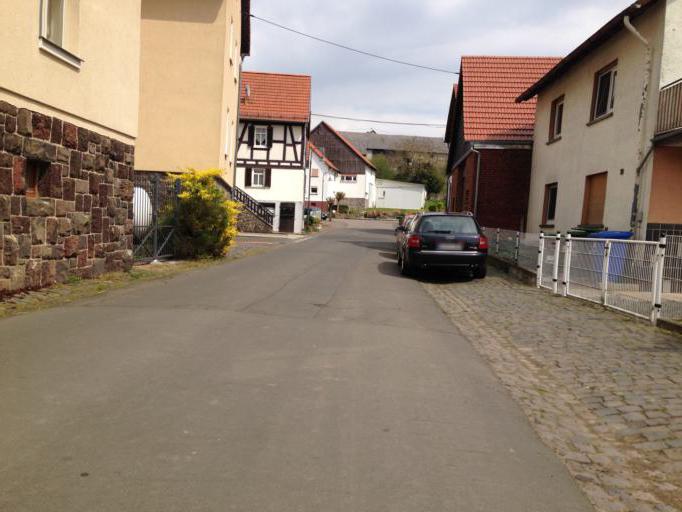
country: DE
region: Hesse
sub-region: Regierungsbezirk Giessen
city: Grunberg
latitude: 50.6106
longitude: 8.9851
